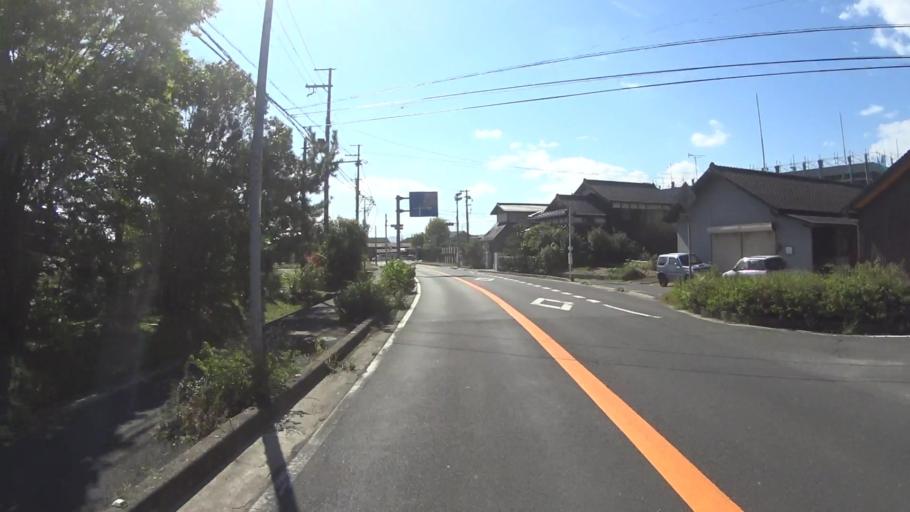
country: JP
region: Kyoto
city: Miyazu
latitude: 35.6321
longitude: 135.0749
